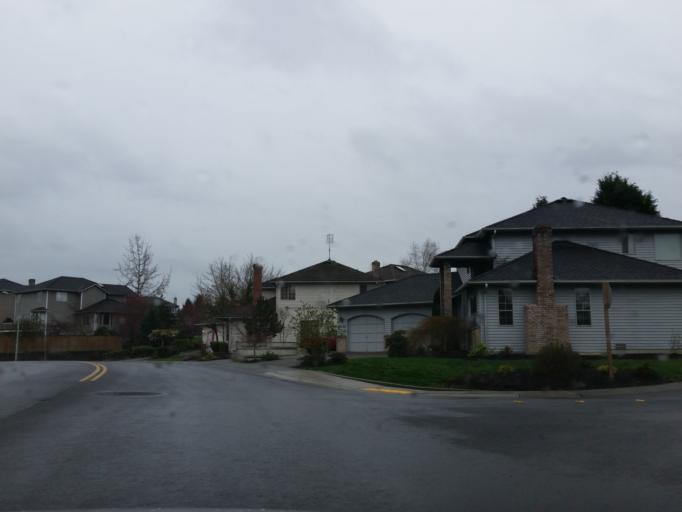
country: US
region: Washington
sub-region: Snohomish County
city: Silver Firs
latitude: 47.8915
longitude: -122.1704
